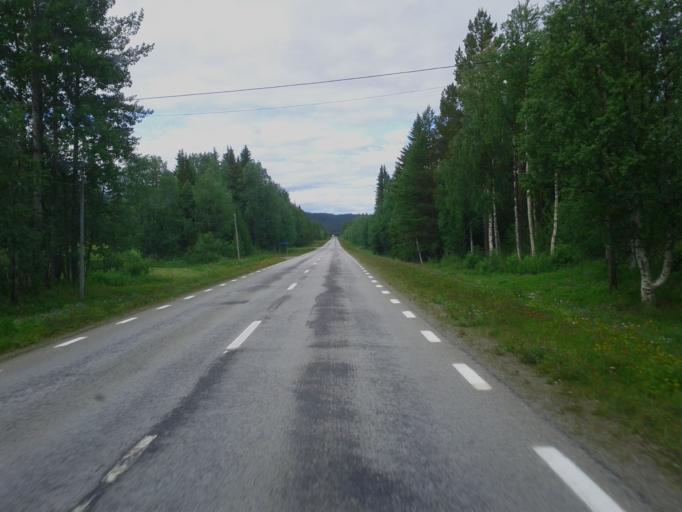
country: SE
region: Vaesterbotten
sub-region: Storumans Kommun
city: Fristad
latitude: 65.3551
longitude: 16.5659
